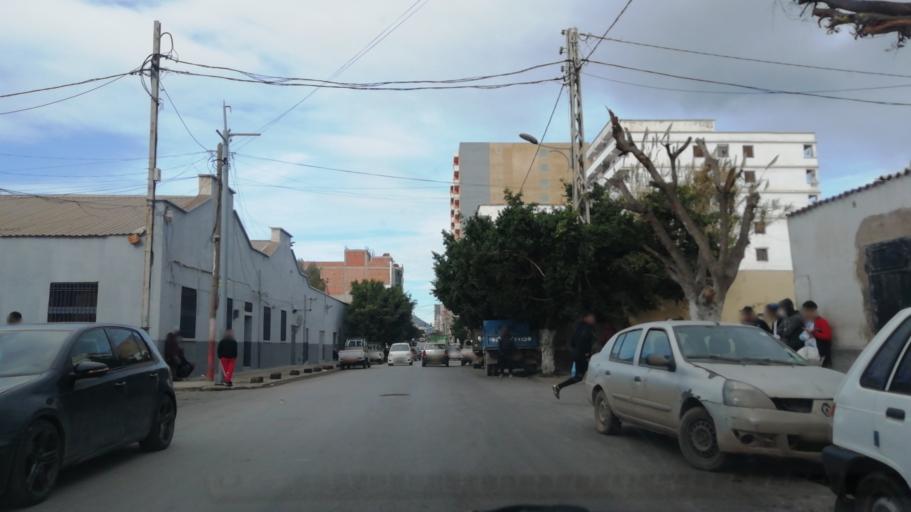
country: DZ
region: Oran
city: Oran
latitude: 35.6875
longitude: -0.6205
